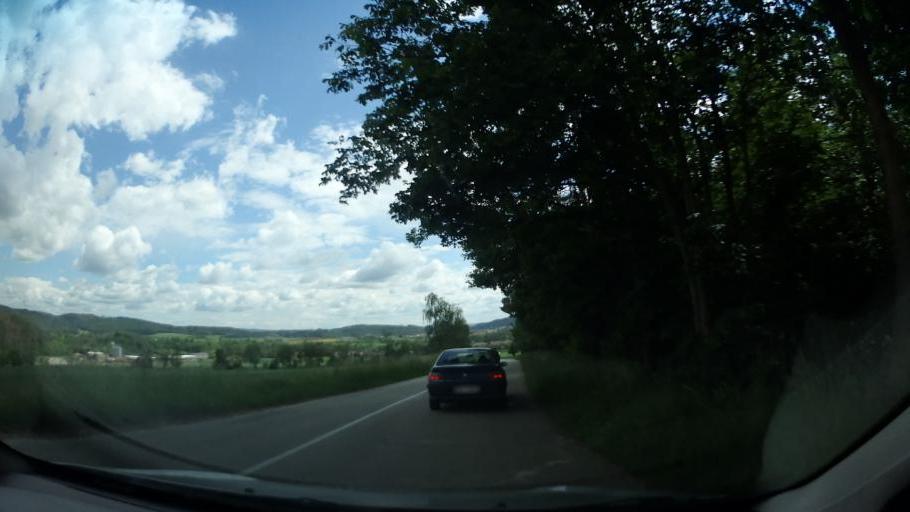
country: CZ
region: South Moravian
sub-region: Okres Blansko
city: Letovice
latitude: 49.5693
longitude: 16.5817
